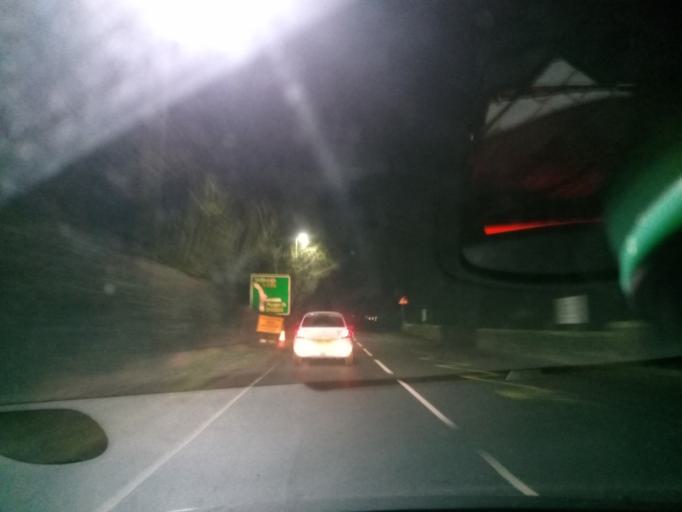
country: GB
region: England
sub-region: Northumberland
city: Meldon
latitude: 55.1041
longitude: -1.8430
